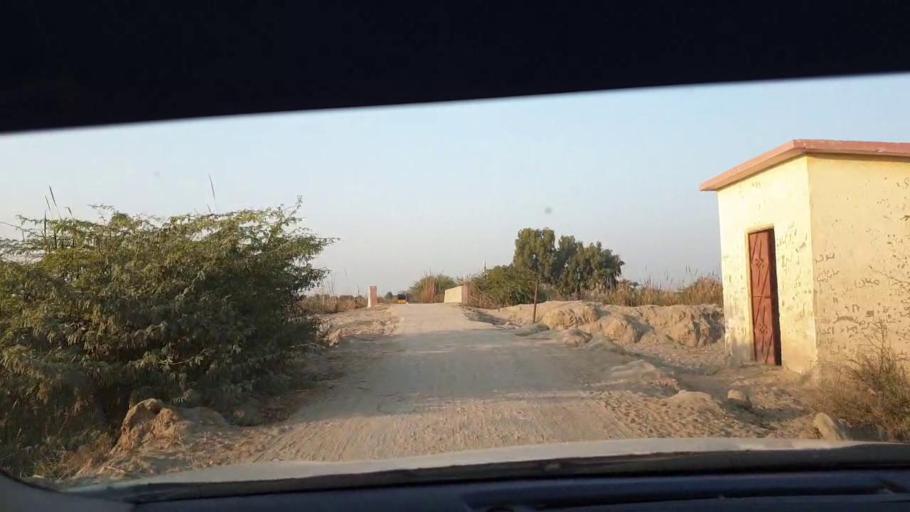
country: PK
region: Sindh
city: Berani
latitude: 25.8586
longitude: 68.8164
